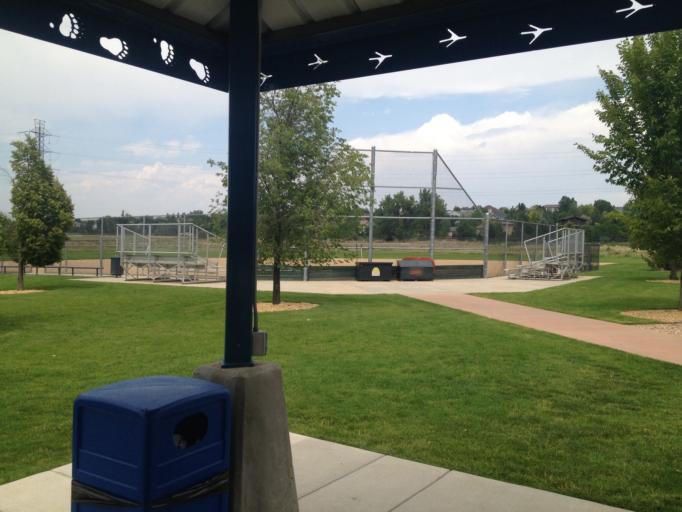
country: US
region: Colorado
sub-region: Boulder County
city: Erie
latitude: 40.0566
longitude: -105.0467
